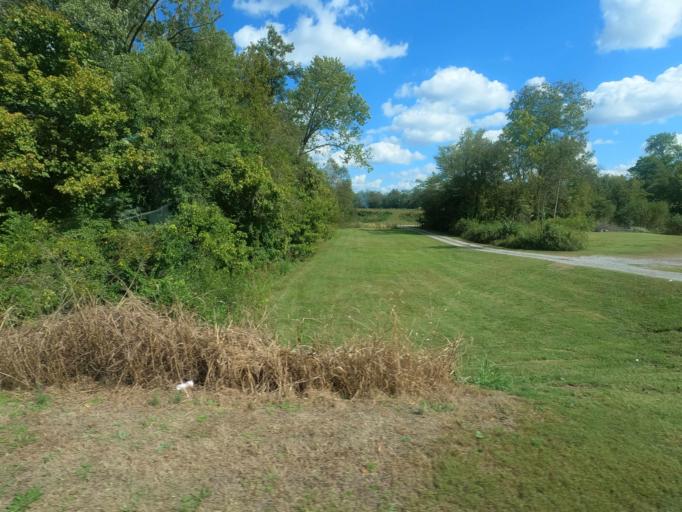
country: US
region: Illinois
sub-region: Johnson County
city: Vienna
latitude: 37.4190
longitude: -88.8931
